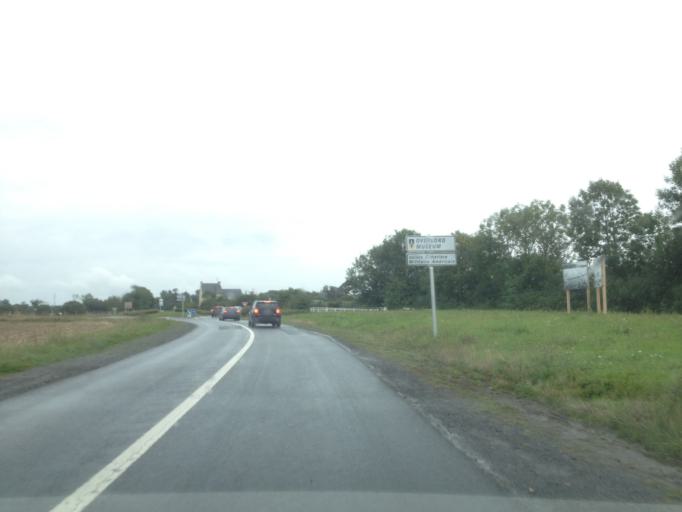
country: FR
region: Lower Normandy
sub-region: Departement du Calvados
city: Saint-Vigor-le-Grand
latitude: 49.3351
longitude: -0.6351
